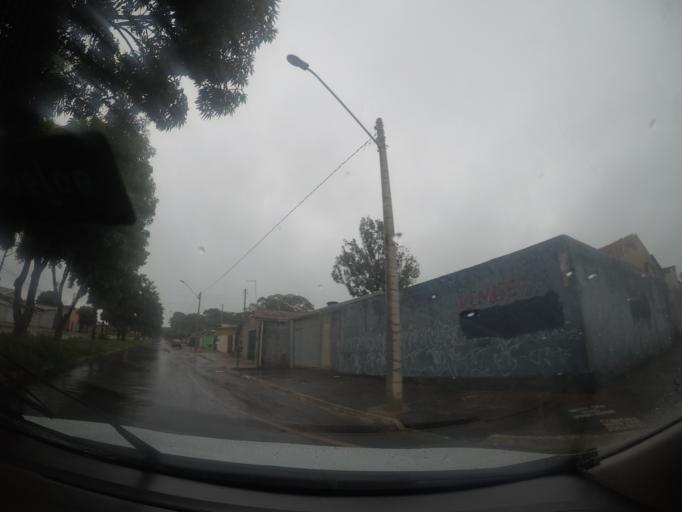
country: BR
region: Goias
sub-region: Goiania
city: Goiania
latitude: -16.5847
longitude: -49.3310
